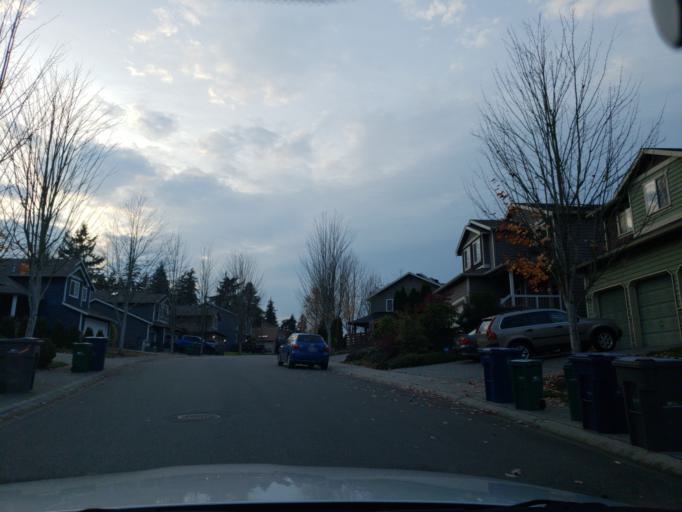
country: US
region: Washington
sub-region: King County
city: Bothell
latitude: 47.7554
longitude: -122.2207
